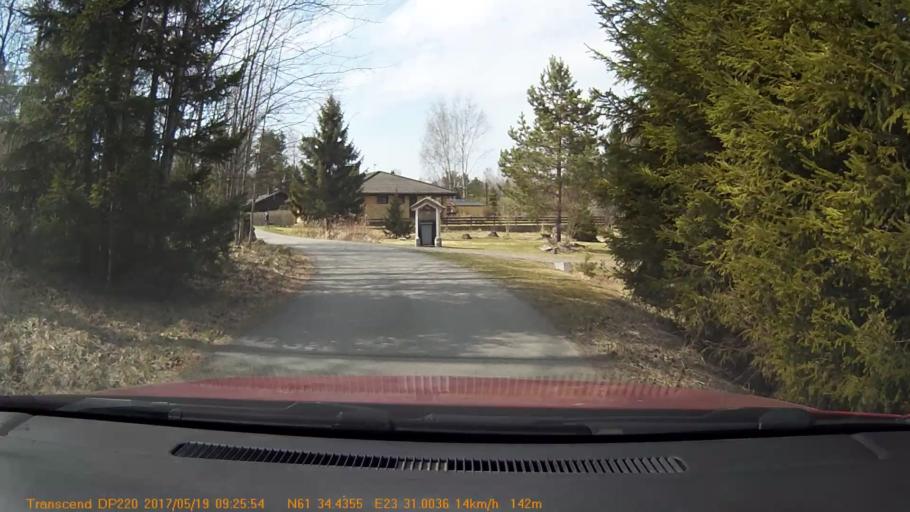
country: FI
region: Pirkanmaa
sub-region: Tampere
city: Yloejaervi
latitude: 61.5740
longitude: 23.5169
